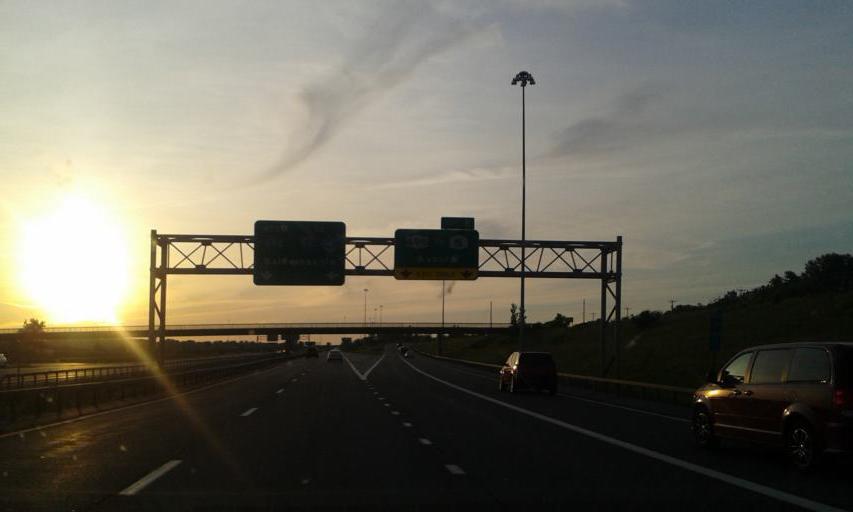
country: US
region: New York
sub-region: Onondaga County
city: Solvay
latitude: 43.0734
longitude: -76.2097
